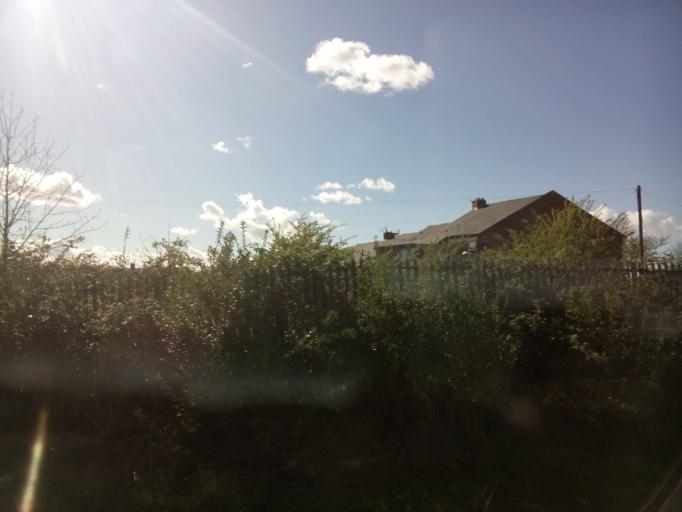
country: GB
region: England
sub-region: Gateshead
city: Gateshead
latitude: 54.9546
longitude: -1.6196
